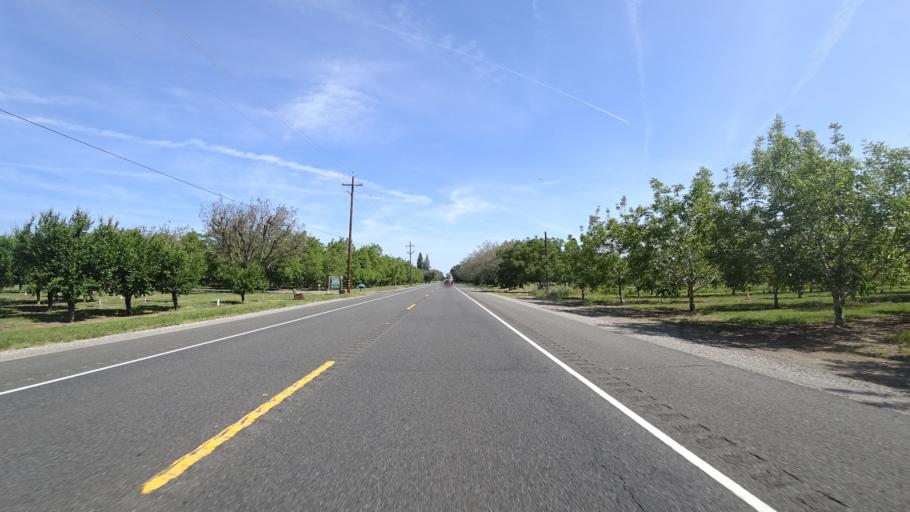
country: US
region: California
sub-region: Tehama County
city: Red Bluff
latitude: 40.1569
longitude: -122.1467
